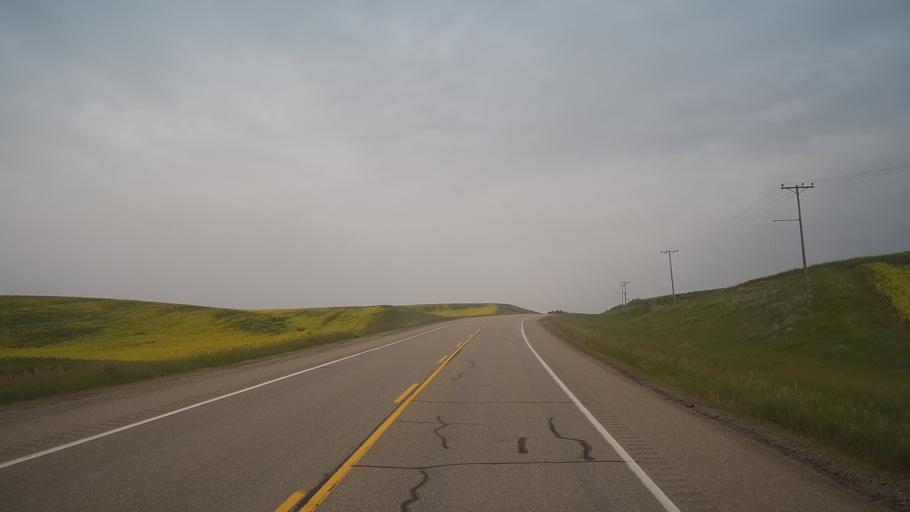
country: CA
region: Saskatchewan
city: Biggar
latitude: 52.0545
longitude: -107.7660
